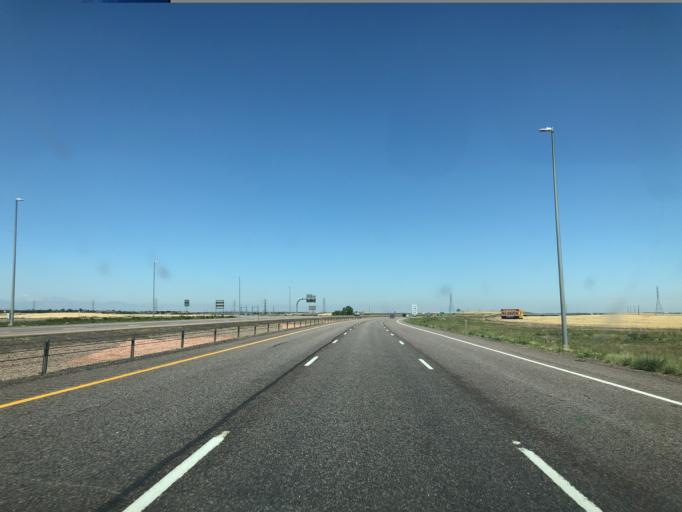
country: US
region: Colorado
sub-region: Adams County
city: Brighton
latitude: 39.8746
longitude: -104.7583
